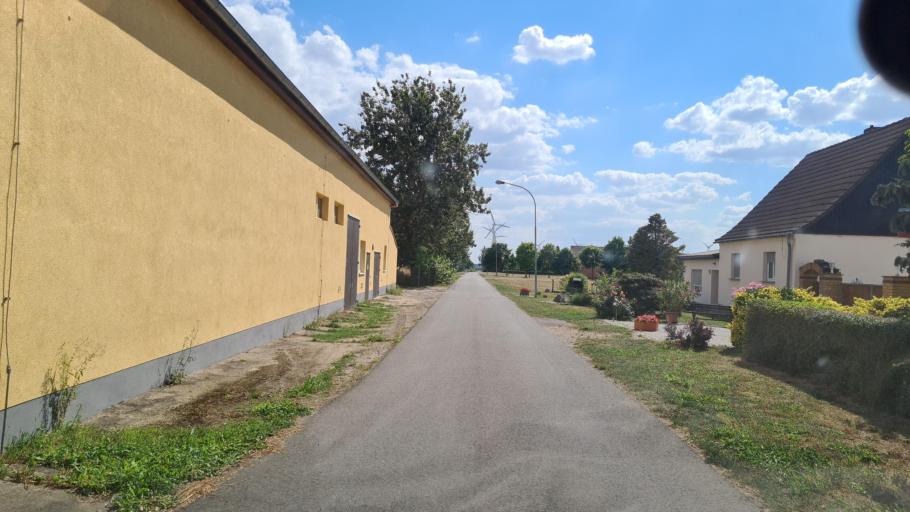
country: DE
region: Saxony-Anhalt
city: Kropstadt
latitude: 52.0133
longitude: 12.8217
